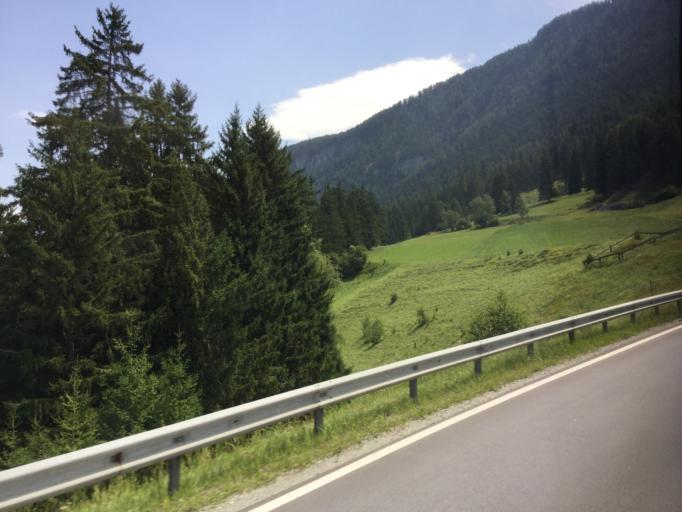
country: CH
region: Grisons
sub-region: Albula District
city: Tiefencastel
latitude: 46.6600
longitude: 9.5828
